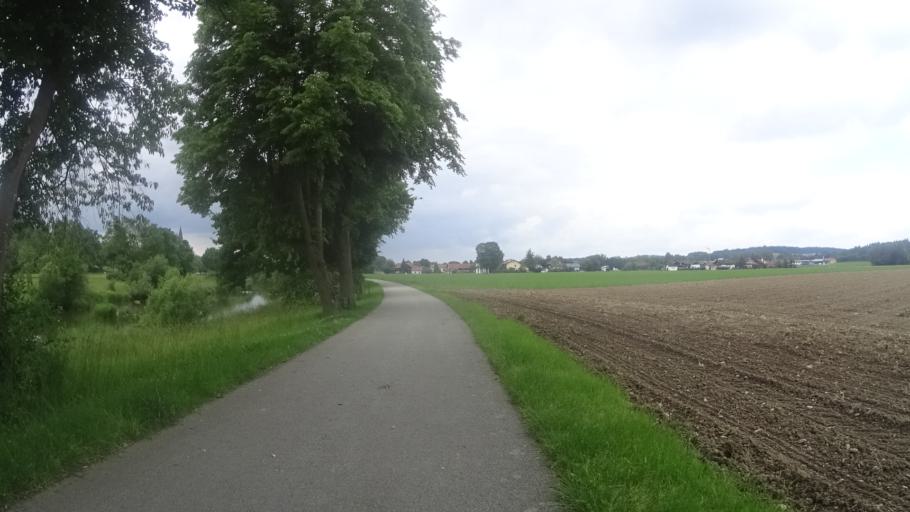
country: DE
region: Bavaria
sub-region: Lower Bavaria
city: Postmunster
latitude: 48.4208
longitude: 12.9121
